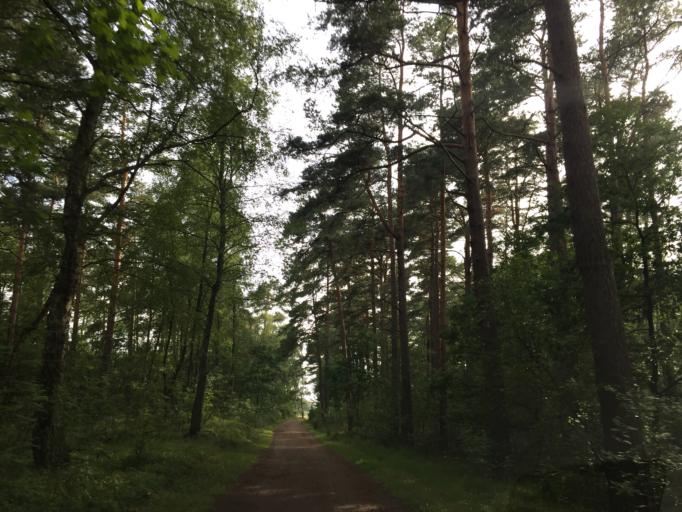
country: SE
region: Halland
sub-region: Falkenbergs Kommun
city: Falkenberg
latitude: 56.8819
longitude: 12.5342
